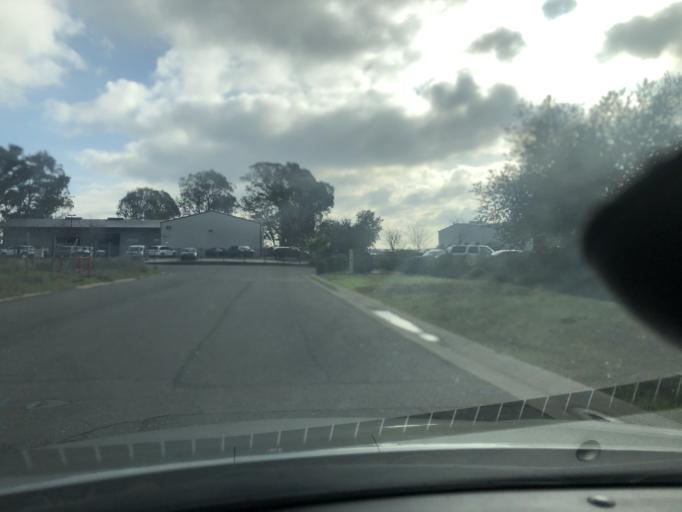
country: US
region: California
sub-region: Sacramento County
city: Florin
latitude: 38.5083
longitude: -121.3755
